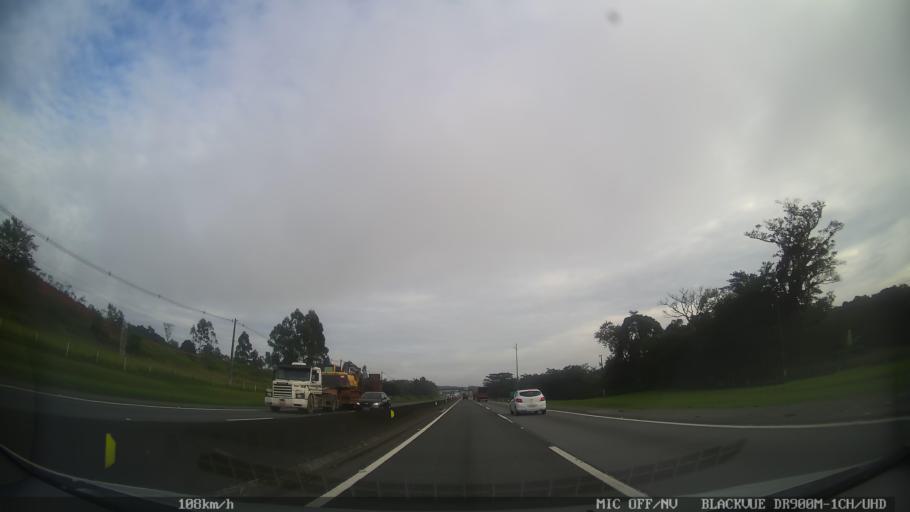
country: BR
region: Santa Catarina
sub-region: Joinville
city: Joinville
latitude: -26.4594
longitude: -48.7573
